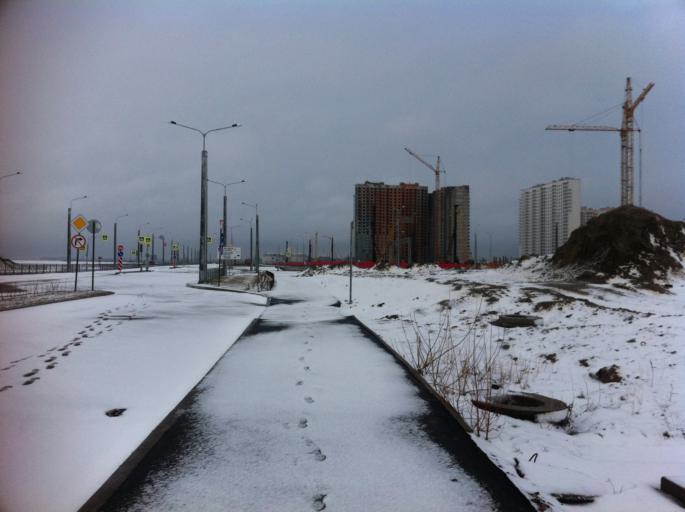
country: RU
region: St.-Petersburg
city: Sosnovaya Polyana
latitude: 59.8662
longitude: 30.1523
